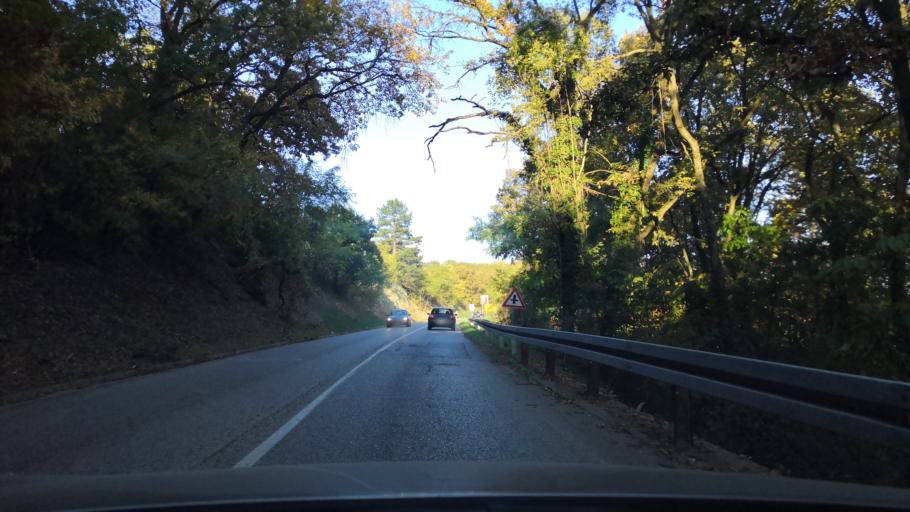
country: RS
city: Vrdnik
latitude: 45.1569
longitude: 19.7764
